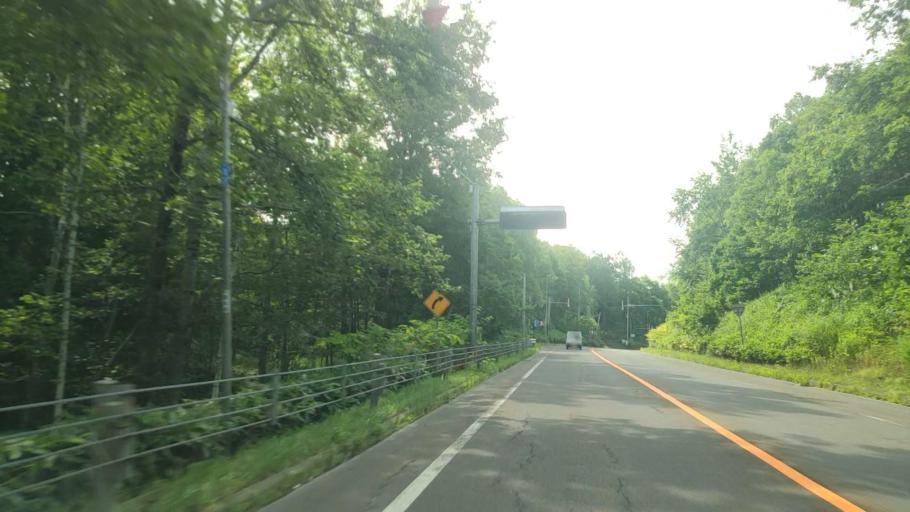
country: JP
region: Hokkaido
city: Nayoro
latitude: 44.3856
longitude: 142.4014
